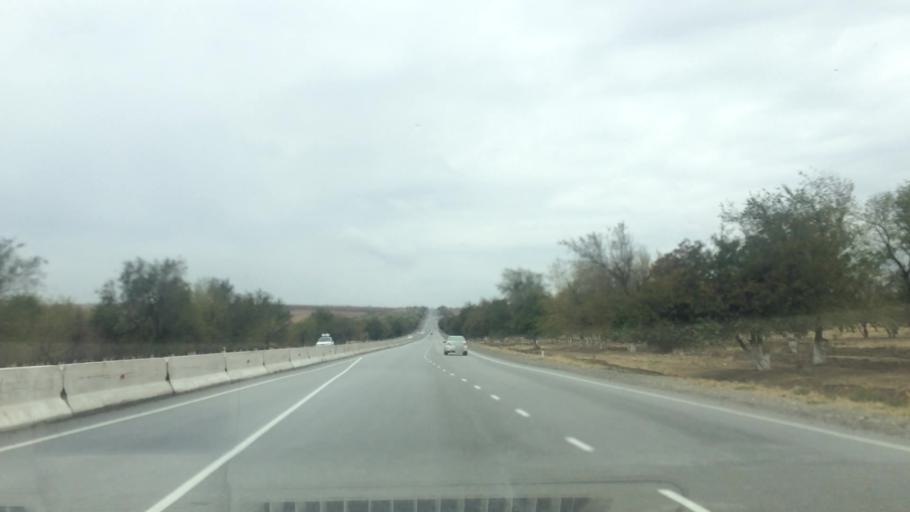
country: UZ
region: Samarqand
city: Bulung'ur
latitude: 39.8764
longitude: 67.4823
